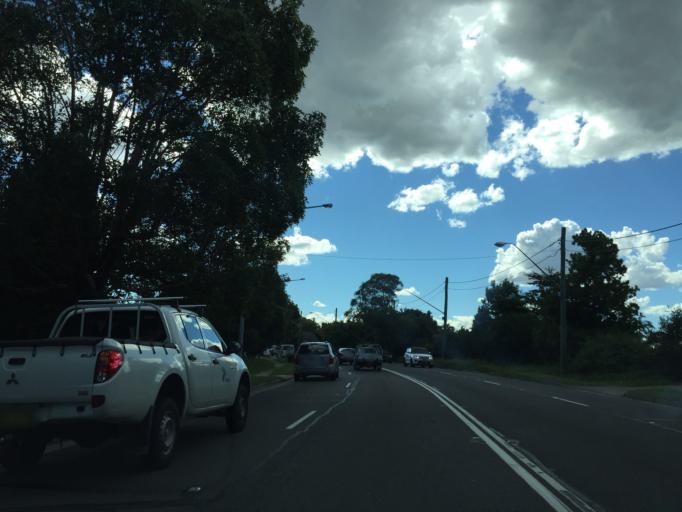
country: AU
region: New South Wales
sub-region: Parramatta
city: Telopea
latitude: -33.7860
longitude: 151.0351
